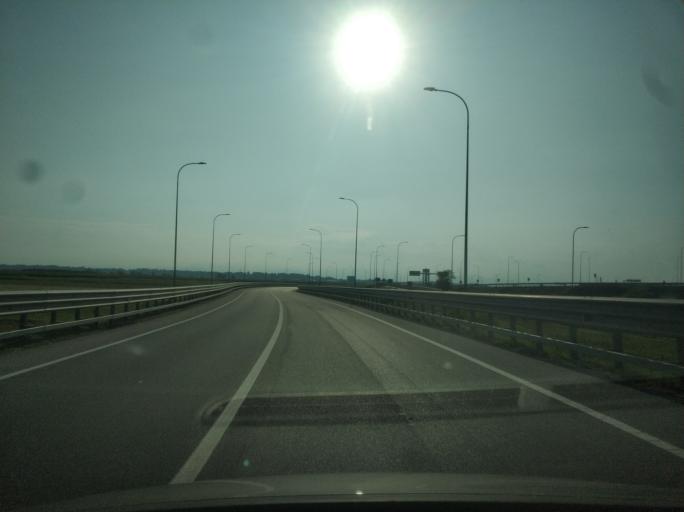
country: IT
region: Piedmont
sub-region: Provincia di Cuneo
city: Roreto
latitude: 44.6633
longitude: 7.8097
